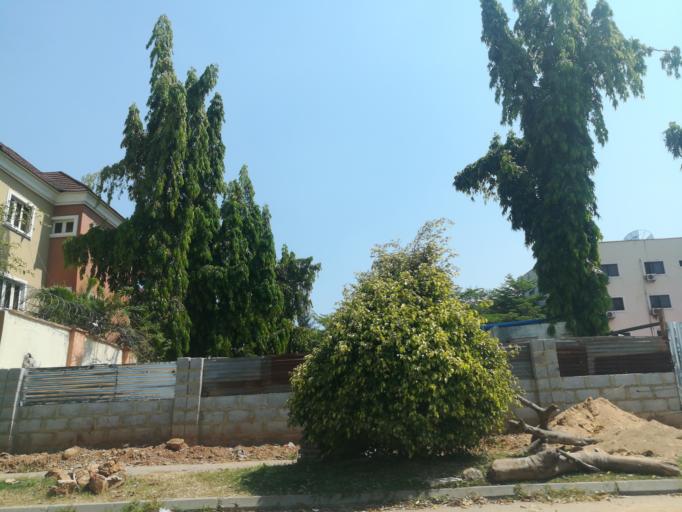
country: NG
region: Abuja Federal Capital Territory
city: Abuja
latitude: 9.0699
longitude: 7.4484
